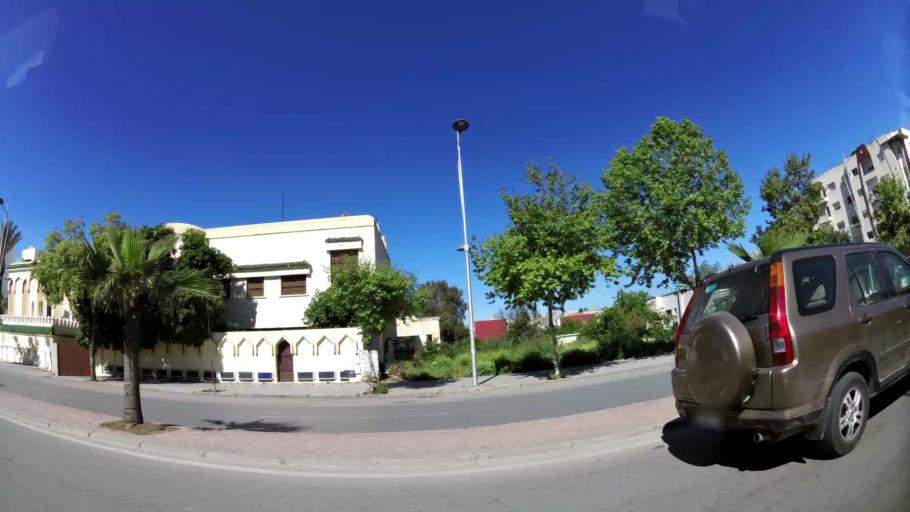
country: MA
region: Fes-Boulemane
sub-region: Fes
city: Fes
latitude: 34.0260
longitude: -4.9905
